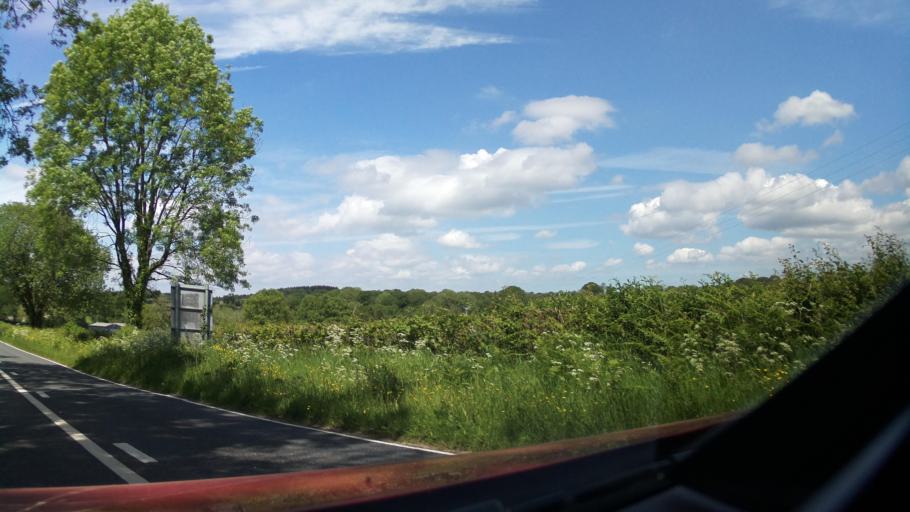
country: GB
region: Wales
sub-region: Monmouthshire
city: Mitchel Troy
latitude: 51.7640
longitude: -2.7249
